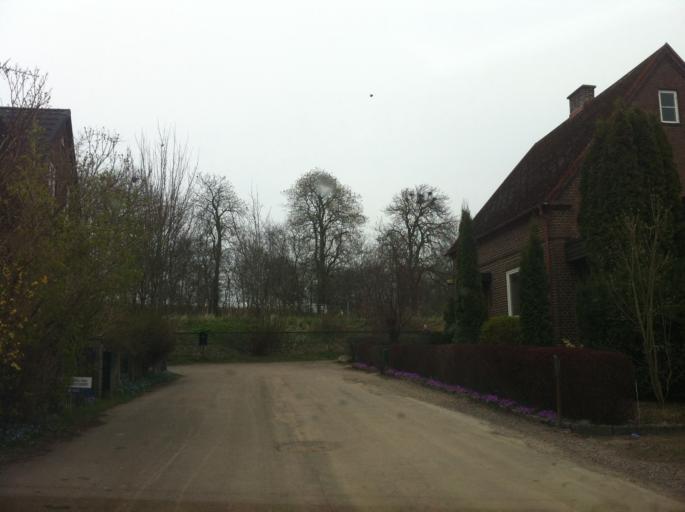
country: SE
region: Skane
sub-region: Svalovs Kommun
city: Kagerod
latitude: 55.9702
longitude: 13.0831
